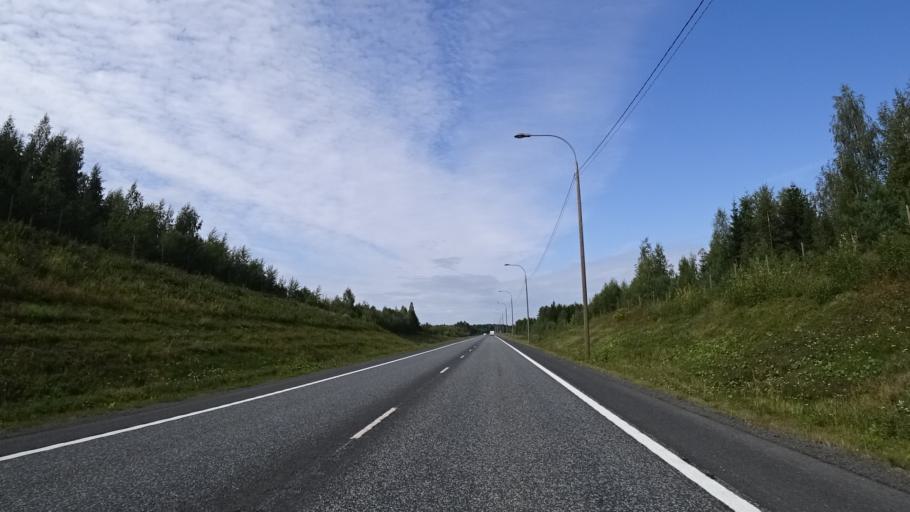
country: FI
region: North Karelia
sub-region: Joensuu
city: Pyhaeselkae
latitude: 62.5247
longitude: 29.8742
